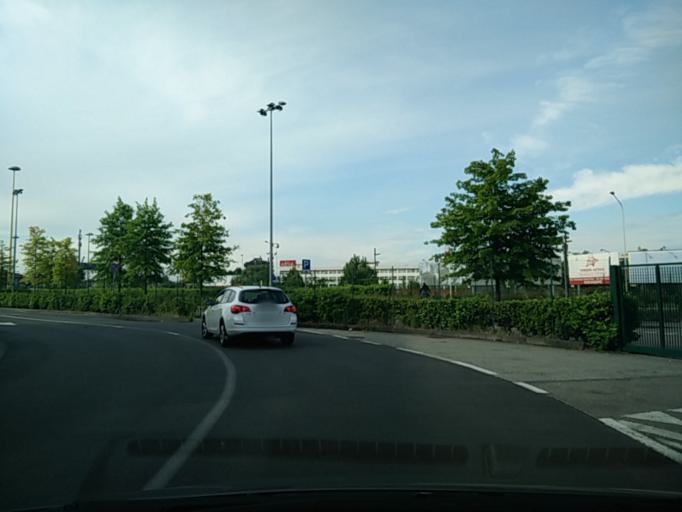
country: IT
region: Lombardy
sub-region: Citta metropolitana di Milano
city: Rho
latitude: 45.5213
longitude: 9.0704
